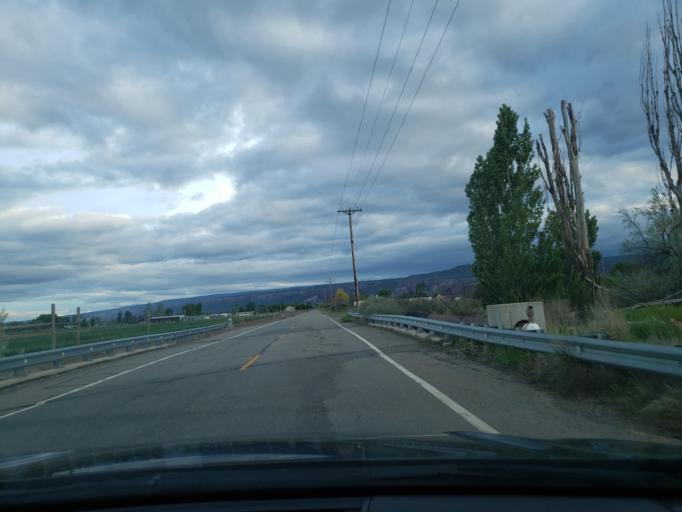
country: US
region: Colorado
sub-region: Mesa County
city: Fruita
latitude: 39.1847
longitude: -108.7012
